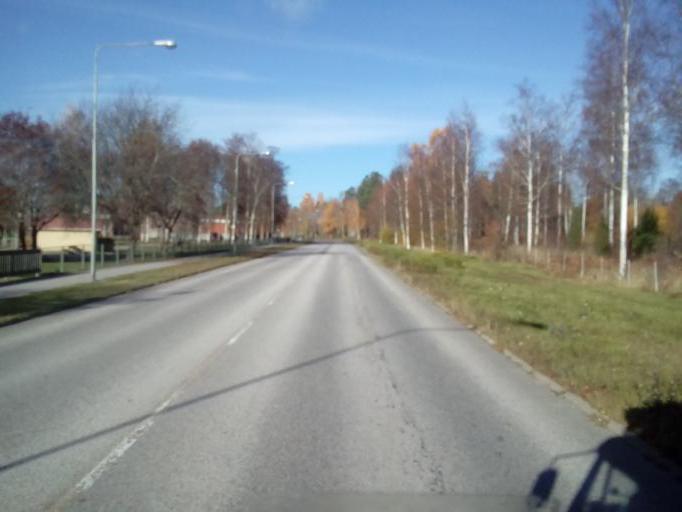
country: SE
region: Kalmar
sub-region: Vimmerby Kommun
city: Vimmerby
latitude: 57.6688
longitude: 15.8745
